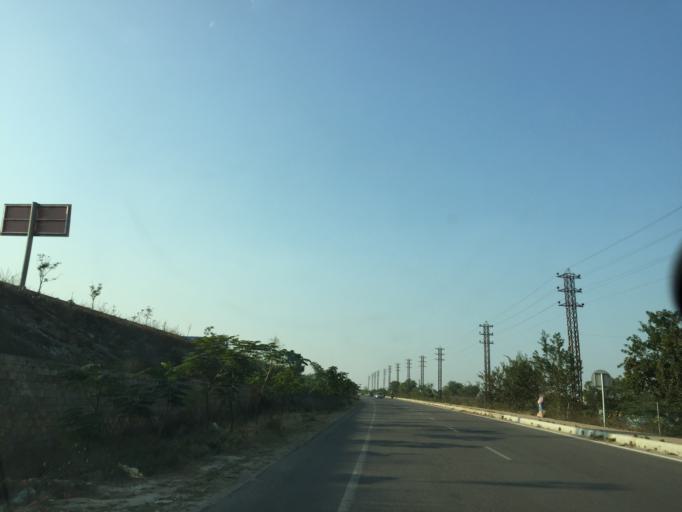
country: IN
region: Telangana
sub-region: Rangareddi
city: Ghatkesar
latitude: 17.4339
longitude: 78.6745
